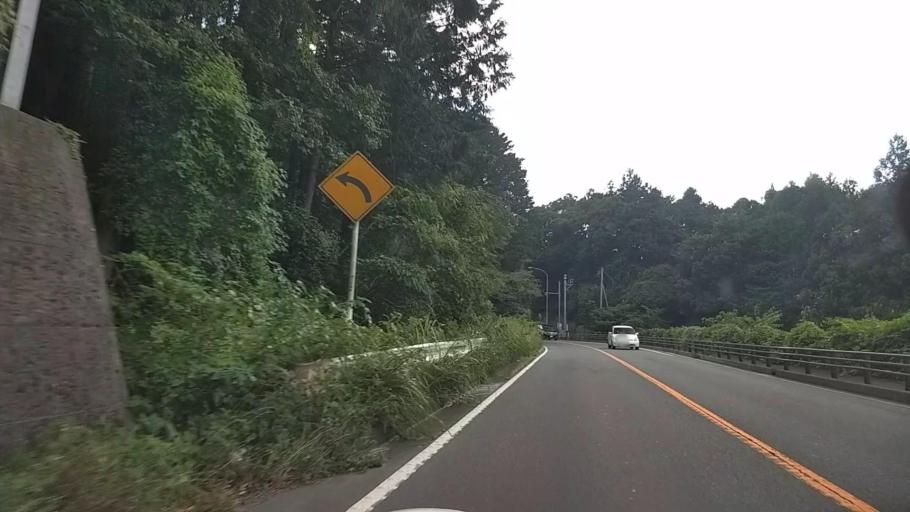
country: JP
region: Shizuoka
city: Fujinomiya
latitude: 35.2170
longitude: 138.5188
